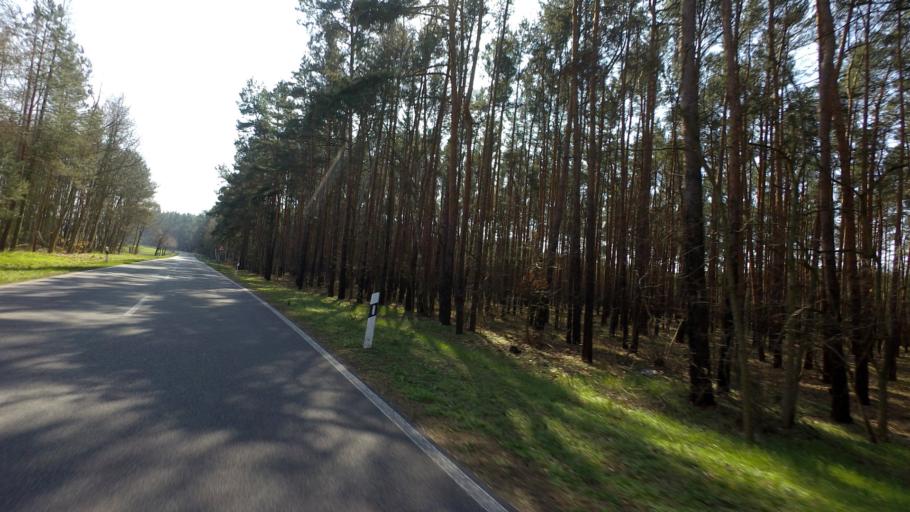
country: DE
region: Brandenburg
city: Golssen
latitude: 51.9550
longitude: 13.5904
